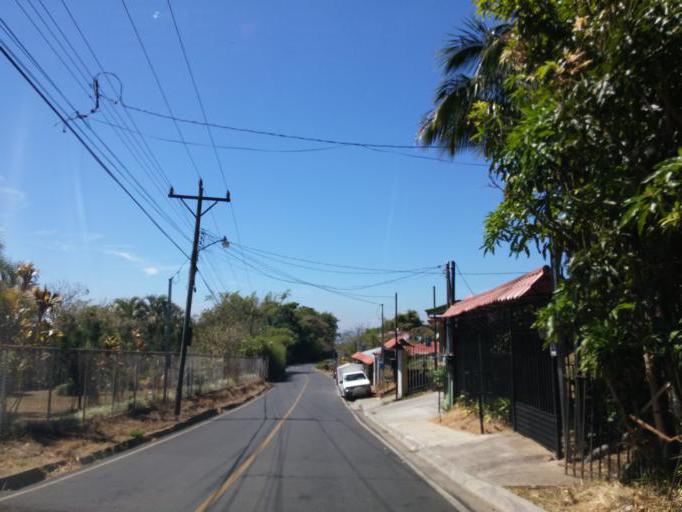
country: CR
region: Alajuela
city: Sabanilla
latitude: 10.0611
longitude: -84.2083
